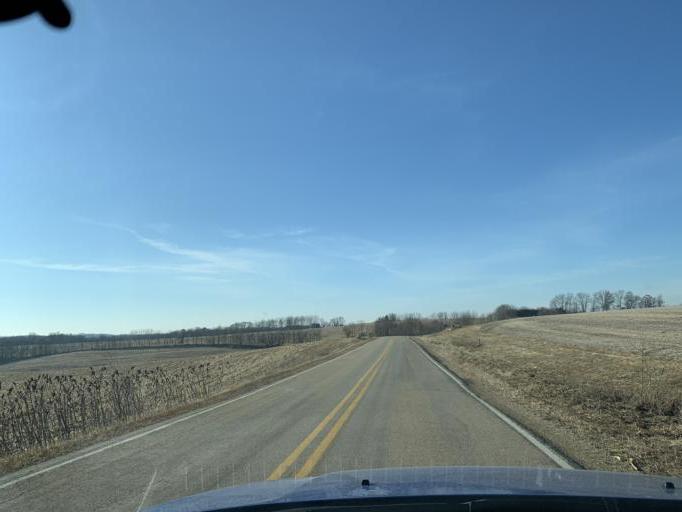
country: US
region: Wisconsin
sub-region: Iowa County
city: Barneveld
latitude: 42.8097
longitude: -89.8874
